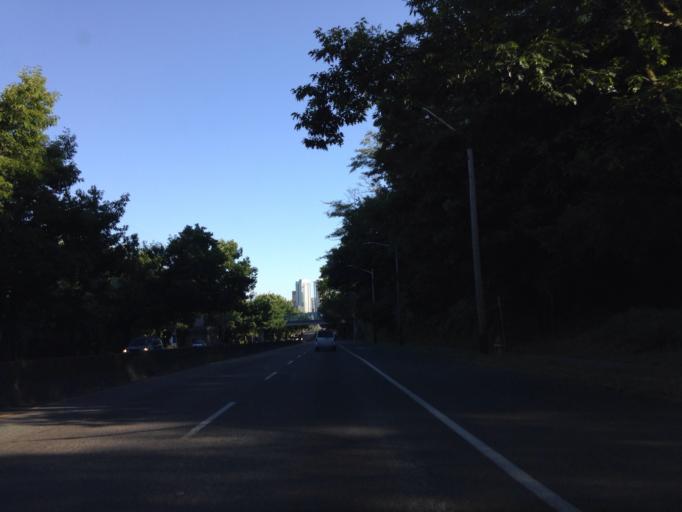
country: US
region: Washington
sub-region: King County
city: Seattle
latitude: 47.6344
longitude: -122.3436
